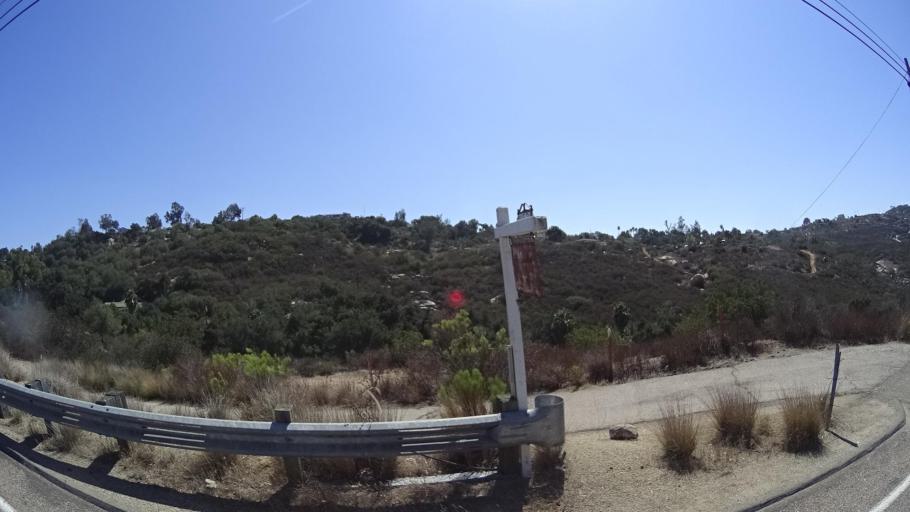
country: US
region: California
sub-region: San Diego County
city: Crest
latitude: 32.8138
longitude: -116.8699
